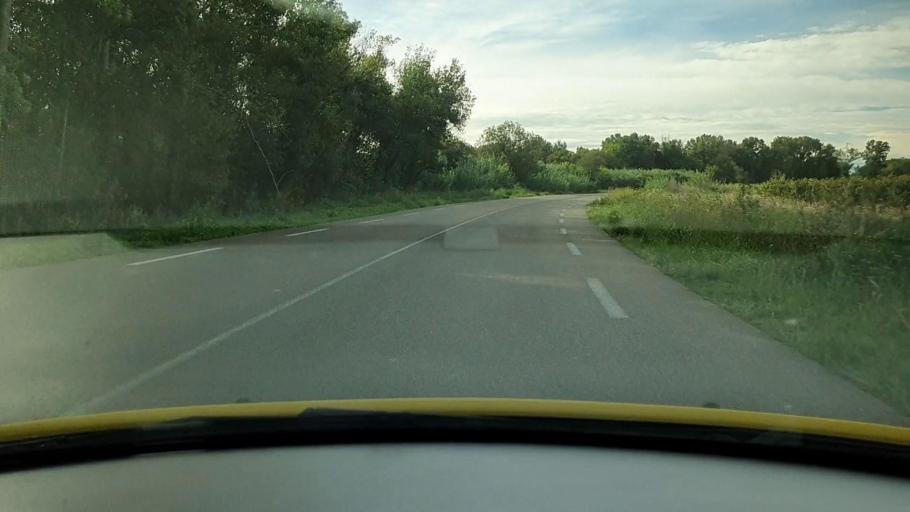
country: FR
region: Languedoc-Roussillon
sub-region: Departement du Gard
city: Bellegarde
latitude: 43.7519
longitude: 4.5297
